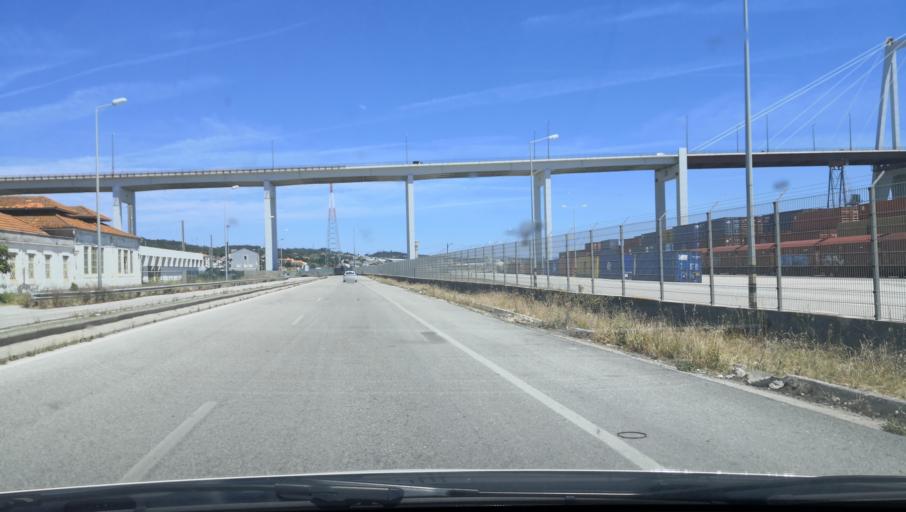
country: PT
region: Coimbra
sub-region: Figueira da Foz
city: Figueira da Foz
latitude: 40.1479
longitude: -8.8447
